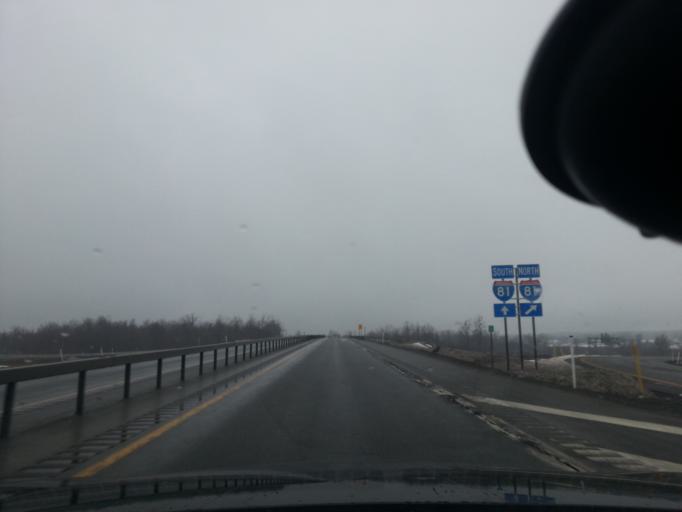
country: US
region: New York
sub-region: Jefferson County
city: Calcium
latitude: 44.0459
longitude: -75.9117
